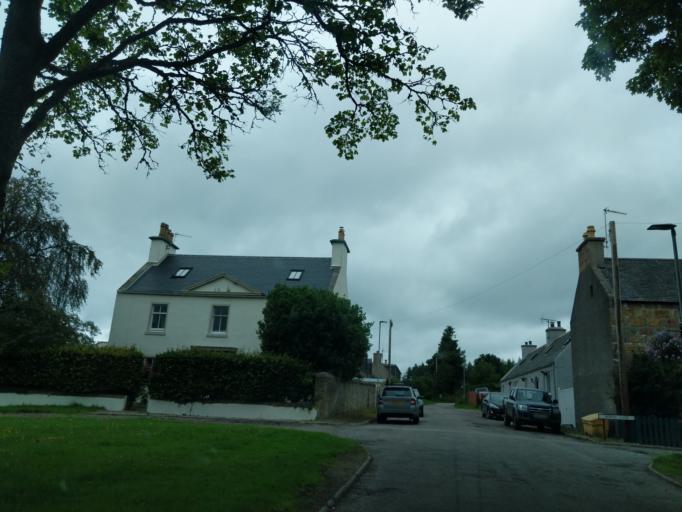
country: GB
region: Scotland
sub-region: Moray
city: Rothes
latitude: 57.4816
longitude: -3.2866
